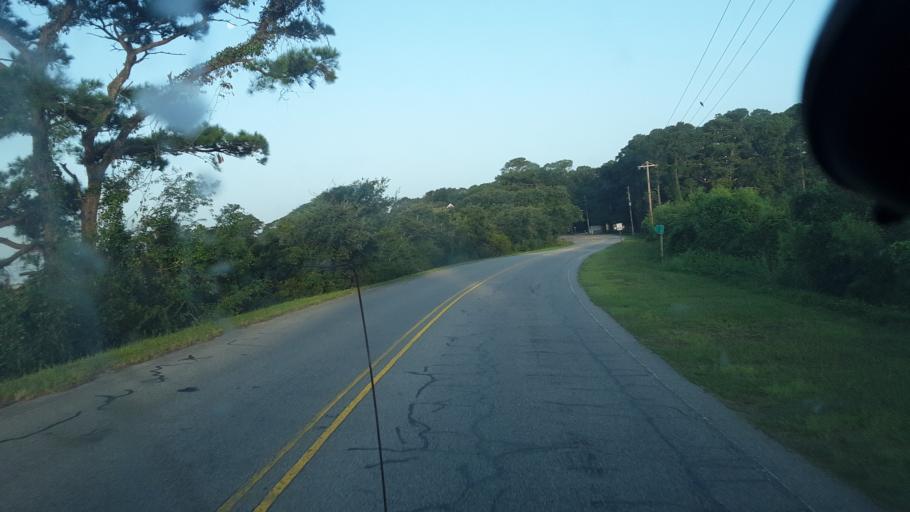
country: US
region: North Carolina
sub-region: Brunswick County
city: Sunset Beach
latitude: 33.8800
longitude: -78.5305
